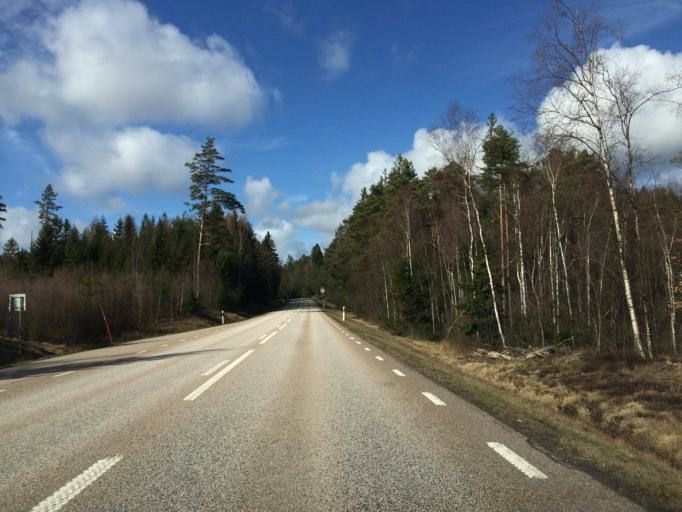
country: SE
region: Kronoberg
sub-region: Markaryds Kommun
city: Markaryd
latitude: 56.4892
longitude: 13.4724
